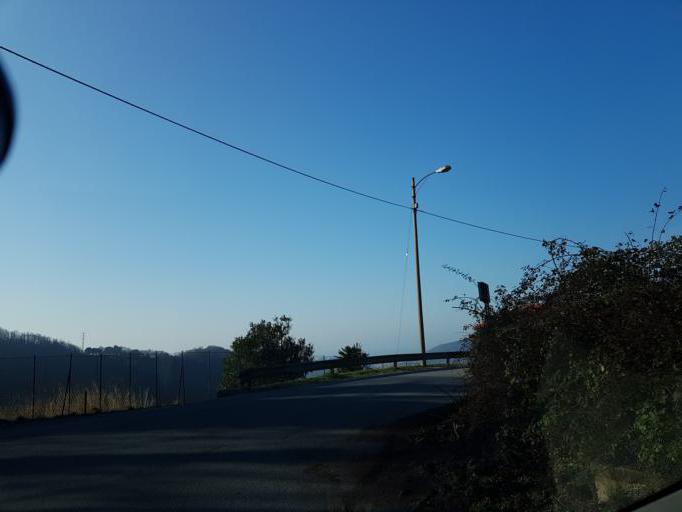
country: IT
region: Liguria
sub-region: Provincia di Genova
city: Manesseno
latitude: 44.4574
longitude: 8.9257
